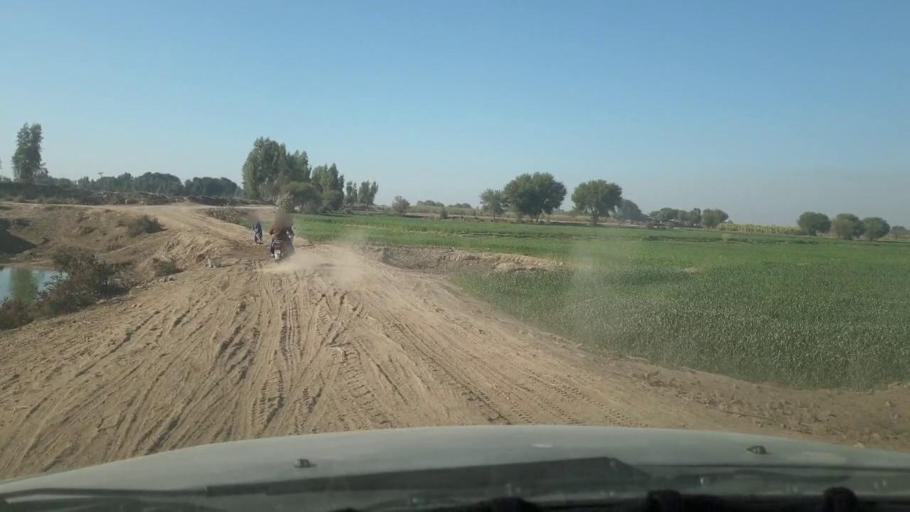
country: PK
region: Sindh
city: Pano Aqil
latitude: 27.9730
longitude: 69.1752
